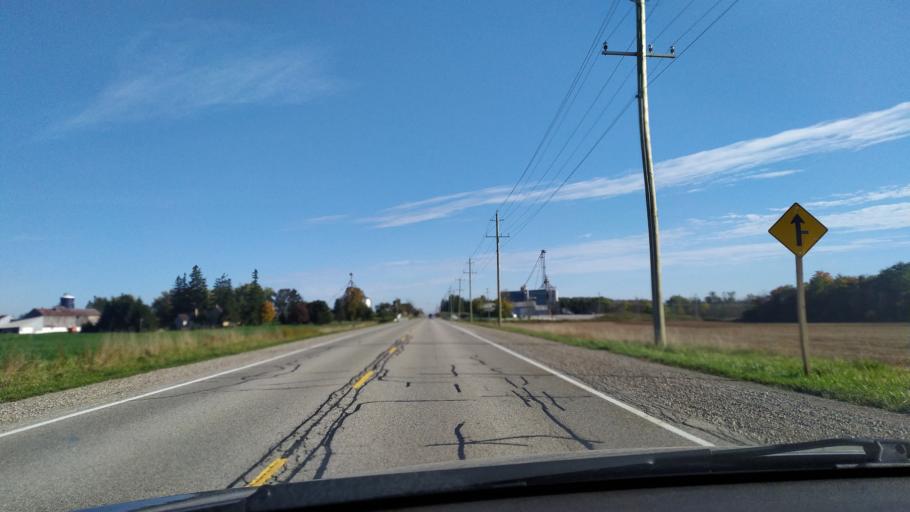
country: CA
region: Ontario
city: Stratford
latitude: 43.4942
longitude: -80.7691
